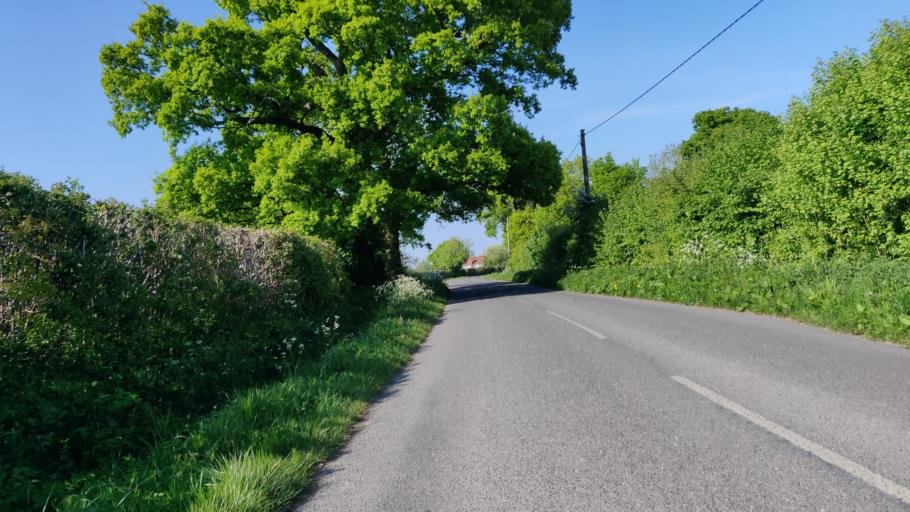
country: GB
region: England
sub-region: West Sussex
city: Southwater
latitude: 51.0387
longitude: -0.3582
